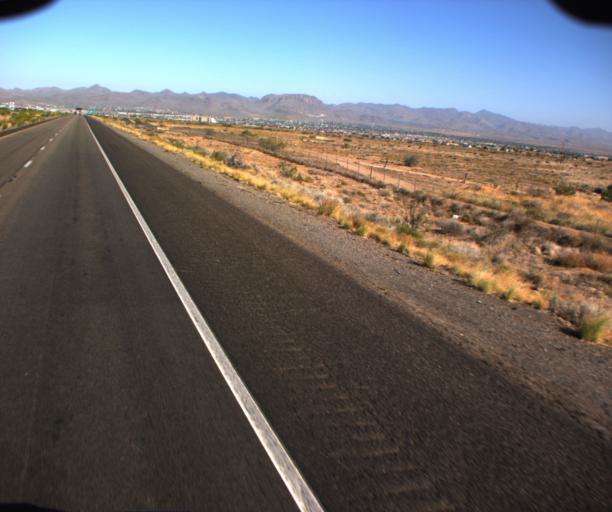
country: US
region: Arizona
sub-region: Mohave County
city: New Kingman-Butler
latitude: 35.2098
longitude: -113.9634
